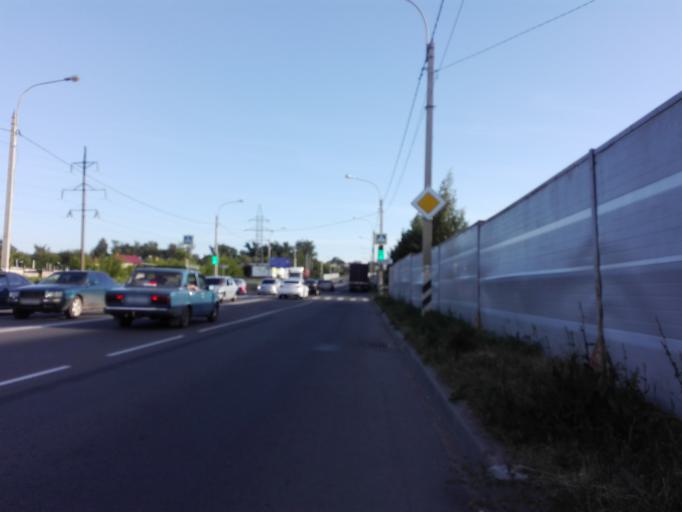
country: RU
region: Orjol
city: Orel
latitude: 52.9544
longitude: 36.0295
